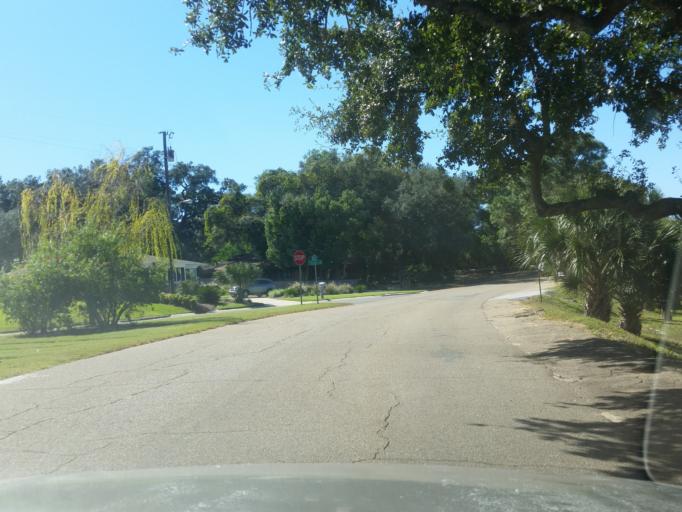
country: US
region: Florida
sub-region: Escambia County
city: East Pensacola Heights
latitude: 30.4306
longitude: -87.1849
